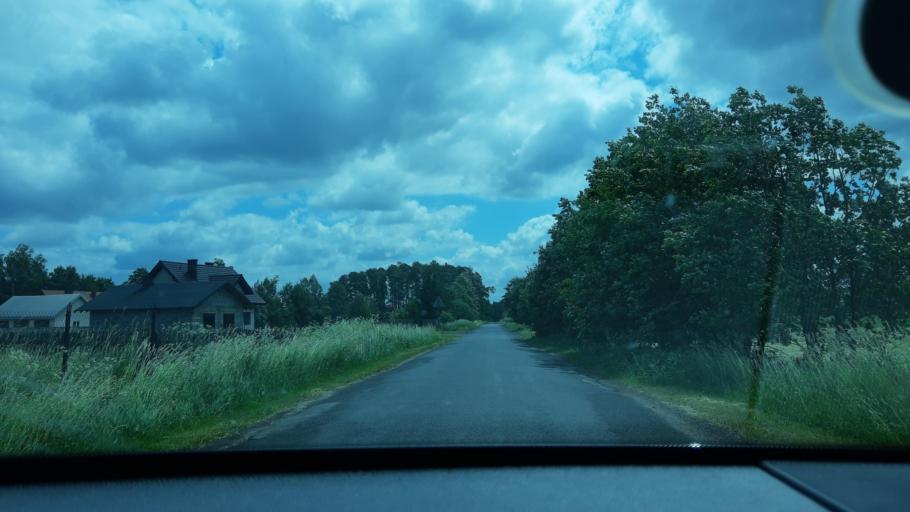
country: PL
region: Lodz Voivodeship
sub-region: Powiat zdunskowolski
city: Zapolice
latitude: 51.5363
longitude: 18.8309
